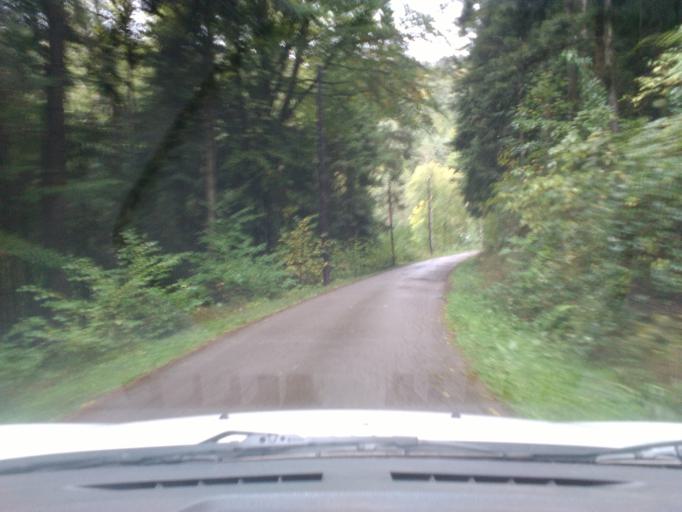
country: FR
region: Lorraine
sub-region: Departement des Vosges
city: Sainte-Marguerite
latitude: 48.3154
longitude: 6.9864
